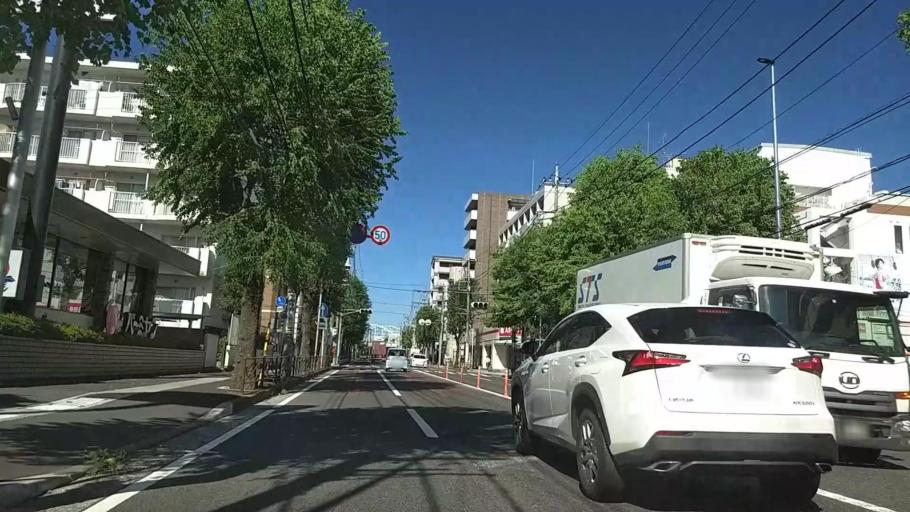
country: JP
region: Tokyo
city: Chofugaoka
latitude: 35.5840
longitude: 139.5844
